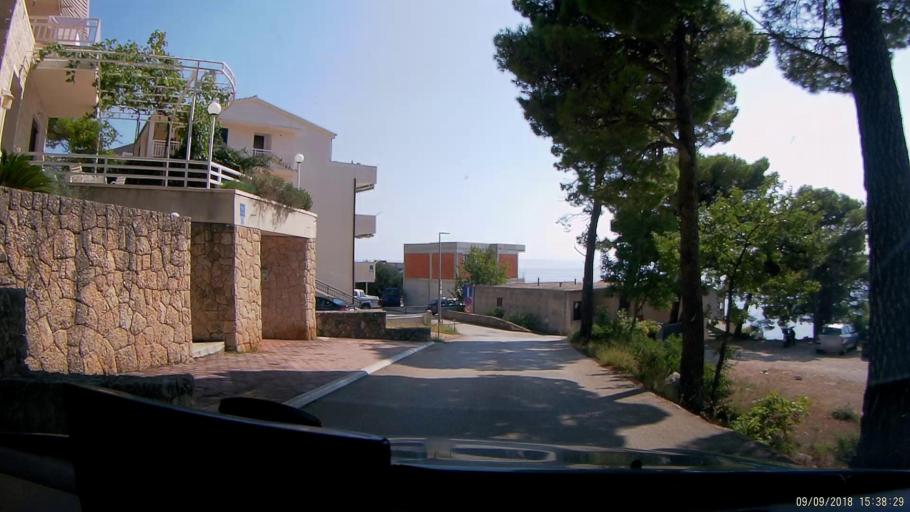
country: HR
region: Splitsko-Dalmatinska
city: Donja Brela
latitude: 43.3702
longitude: 16.9314
